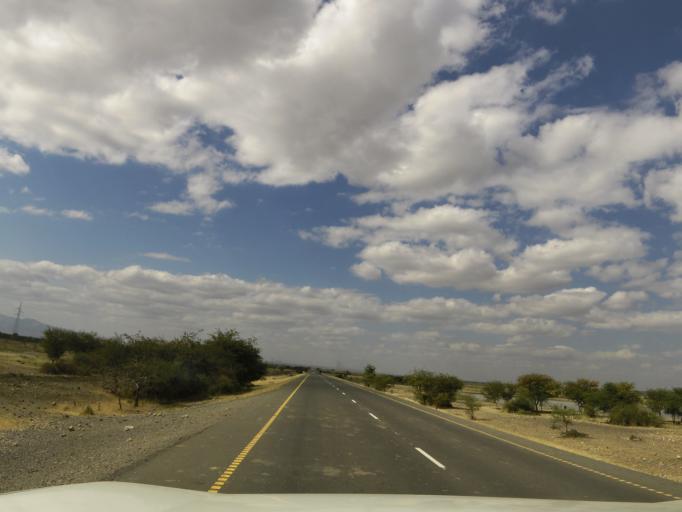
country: TZ
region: Arusha
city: Mto wa Mbu
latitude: -3.6277
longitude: 36.0183
